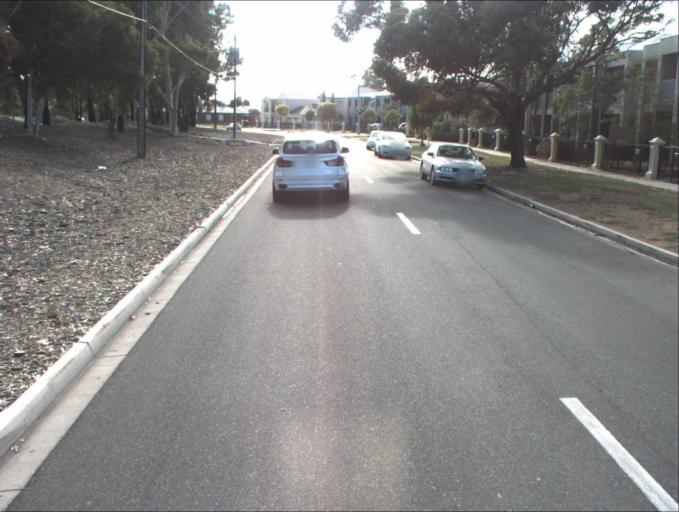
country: AU
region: South Australia
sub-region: Charles Sturt
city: Woodville North
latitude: -34.8604
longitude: 138.5521
